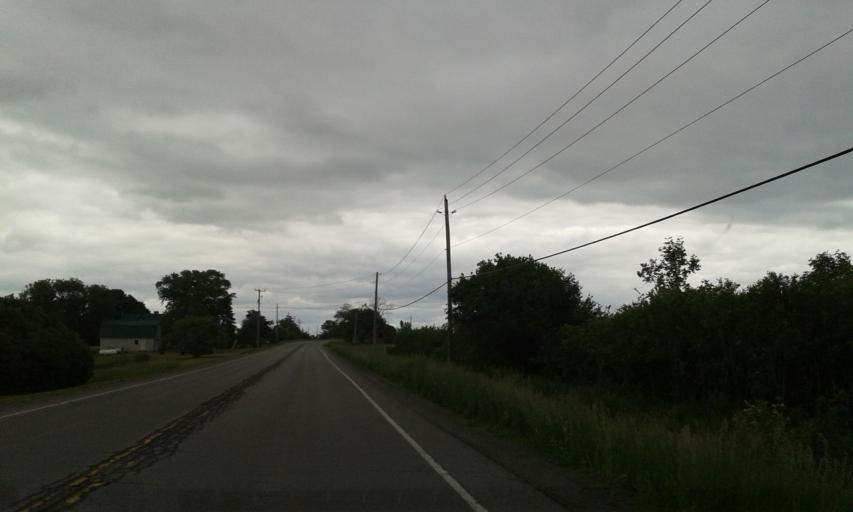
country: CA
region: Ontario
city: Prince Edward
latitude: 43.9716
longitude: -77.4489
